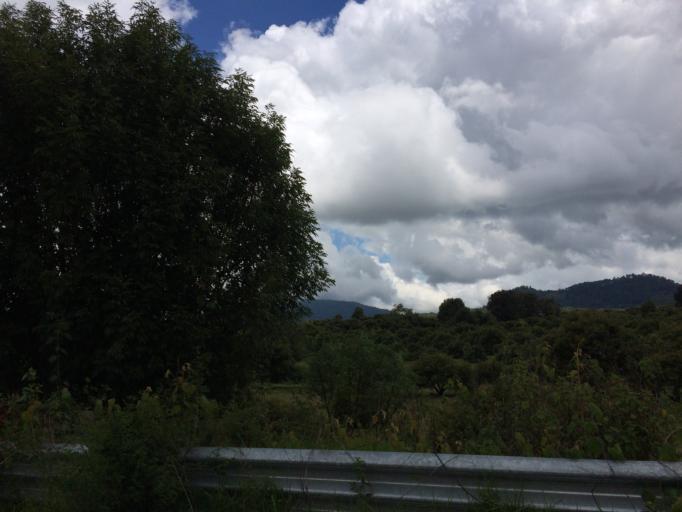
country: MX
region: Michoacan
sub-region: Uruapan
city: Santa Ana Zirosto
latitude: 19.5583
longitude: -102.2942
